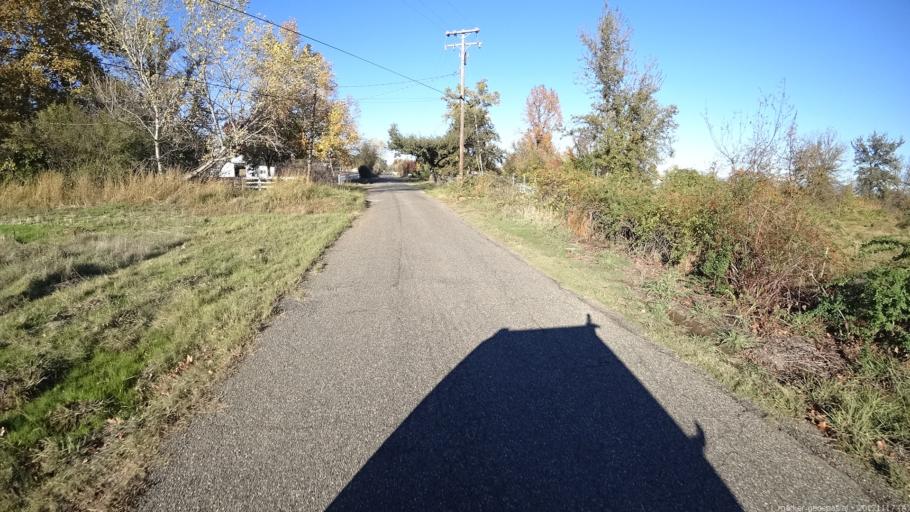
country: US
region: California
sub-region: Shasta County
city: Cottonwood
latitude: 40.3947
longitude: -122.2171
